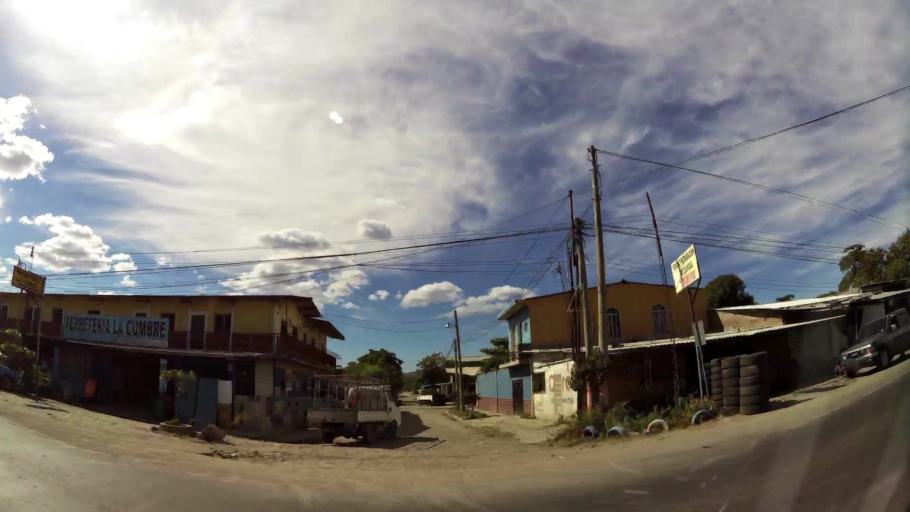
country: SV
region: San Salvador
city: Aguilares
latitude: 13.9595
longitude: -89.1839
